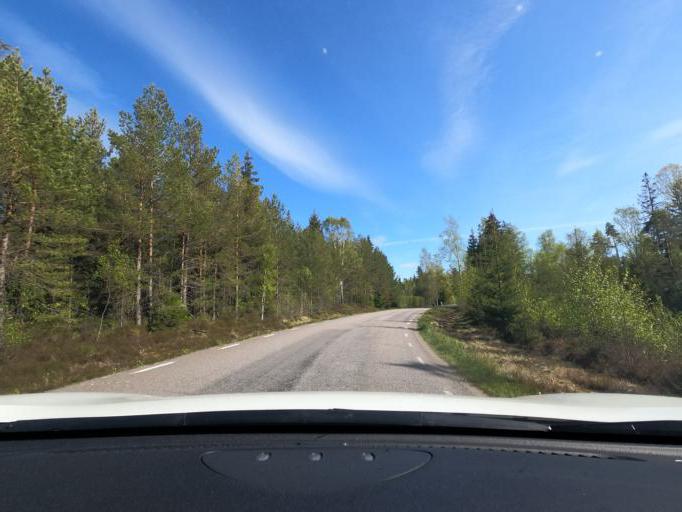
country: SE
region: Vaestra Goetaland
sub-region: Harryda Kommun
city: Hindas
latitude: 57.6693
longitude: 12.3527
